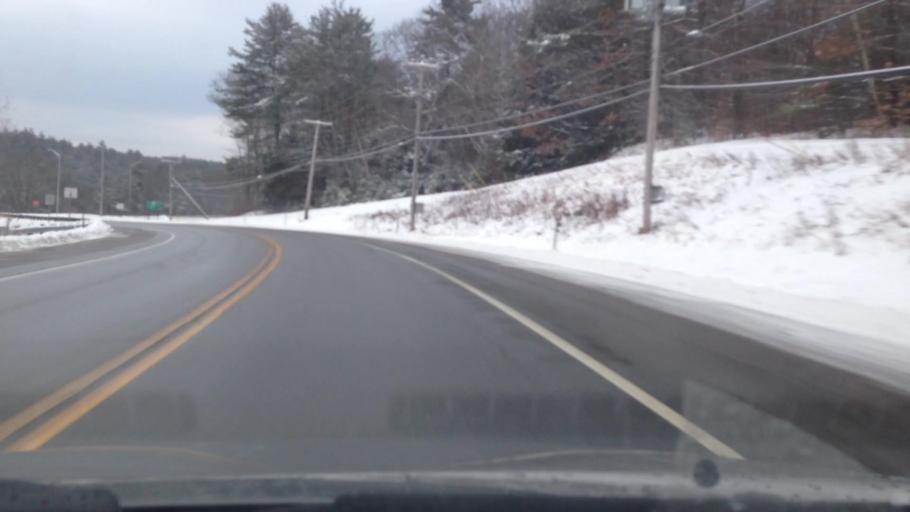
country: US
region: New Hampshire
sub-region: Cheshire County
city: Keene
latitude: 42.9688
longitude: -72.2618
